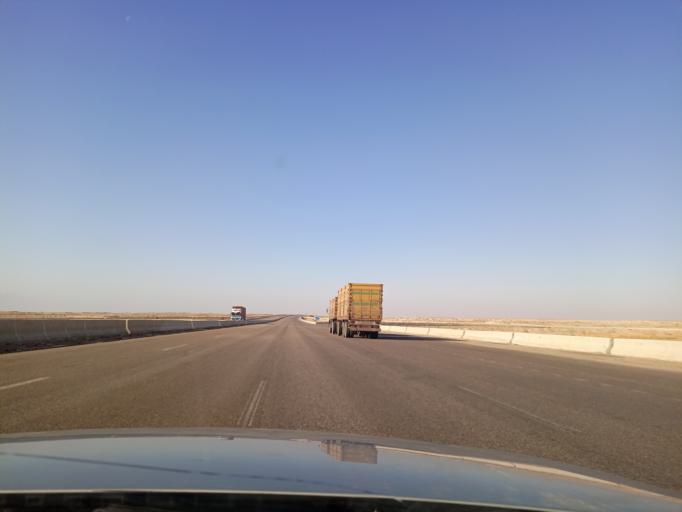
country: EG
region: Muhafazat al Fayyum
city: Tamiyah
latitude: 29.6254
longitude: 30.9580
